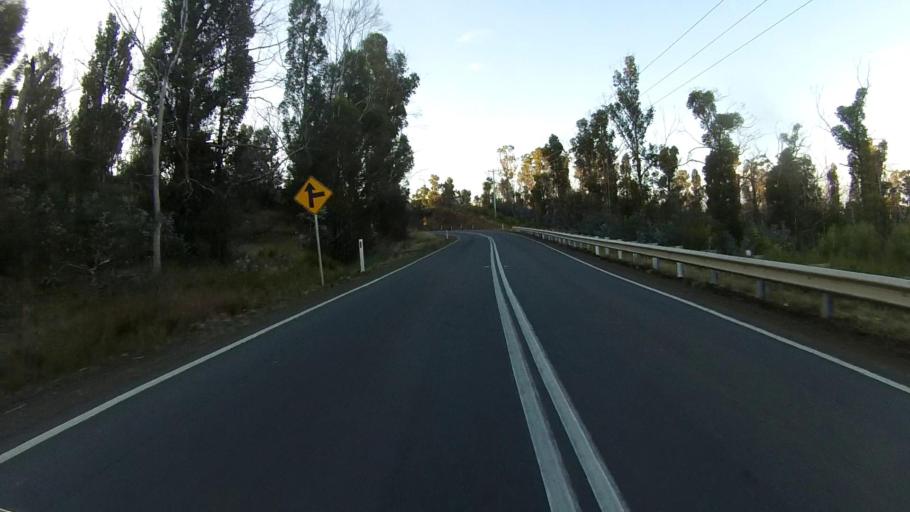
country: AU
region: Tasmania
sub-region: Sorell
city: Sorell
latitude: -42.8543
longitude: 147.8222
